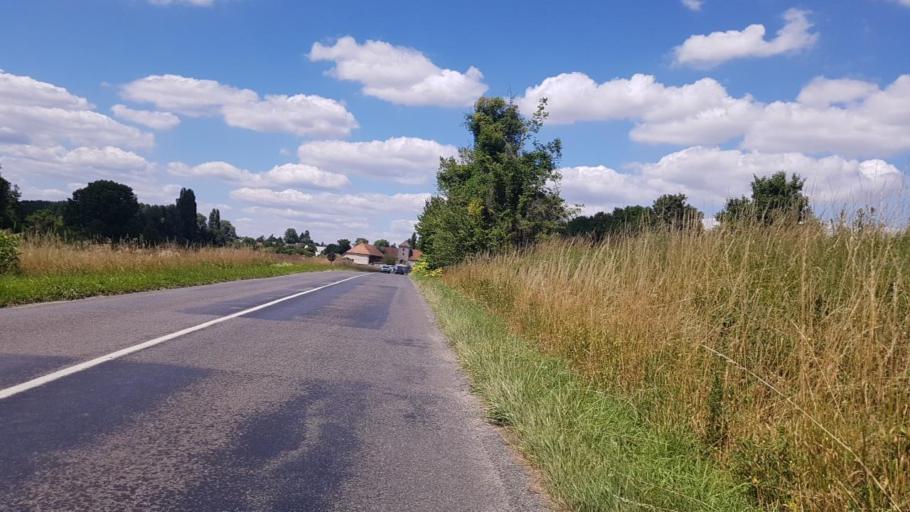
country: FR
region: Ile-de-France
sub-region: Departement de Seine-et-Marne
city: Juilly
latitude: 49.0027
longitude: 2.6690
